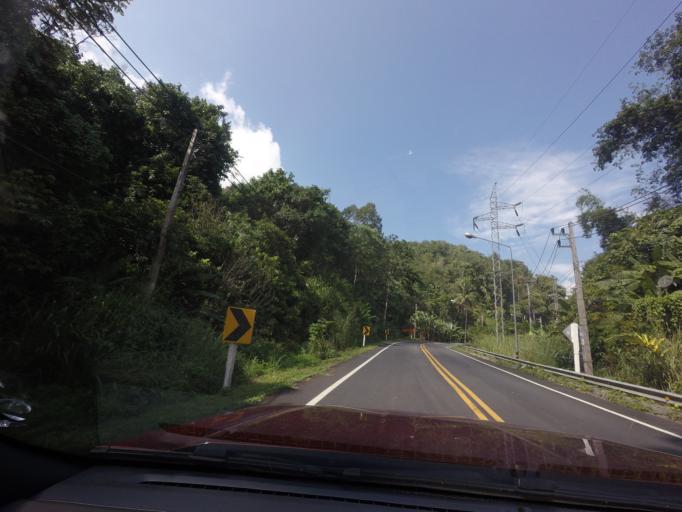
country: TH
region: Yala
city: Betong
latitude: 5.9043
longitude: 101.1486
